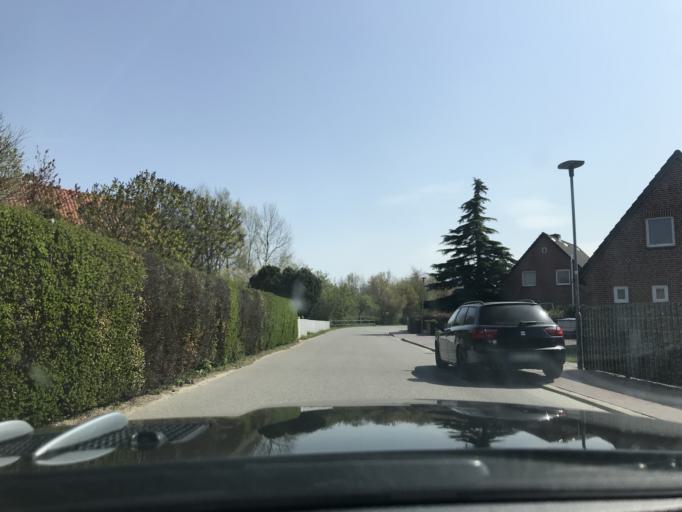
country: DE
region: Schleswig-Holstein
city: Grossenbrode
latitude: 54.3669
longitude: 11.0880
